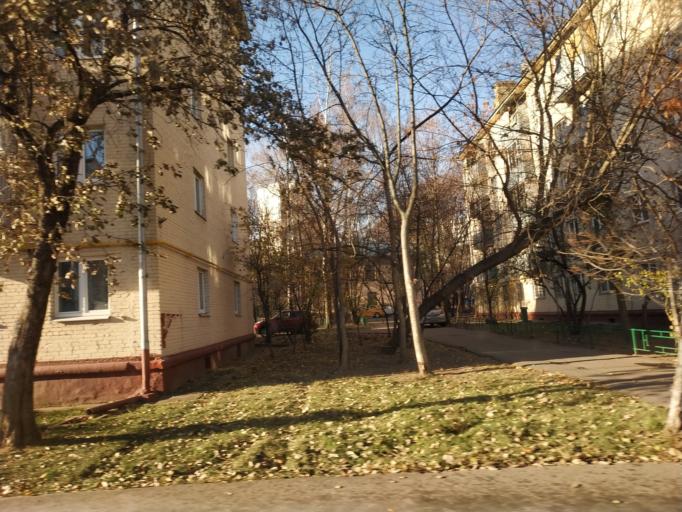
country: RU
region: Moscow
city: Biryulevo
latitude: 55.5803
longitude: 37.6769
